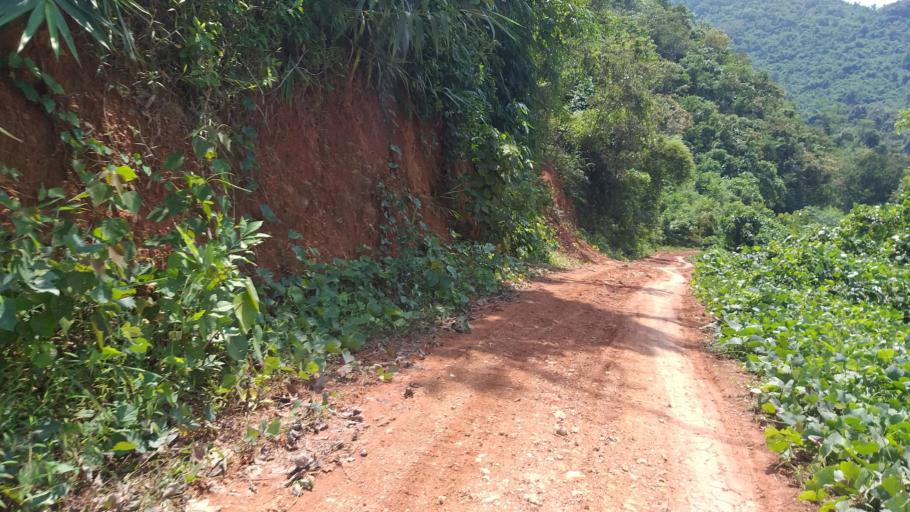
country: LA
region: Phongsali
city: Khoa
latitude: 21.3056
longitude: 102.5591
